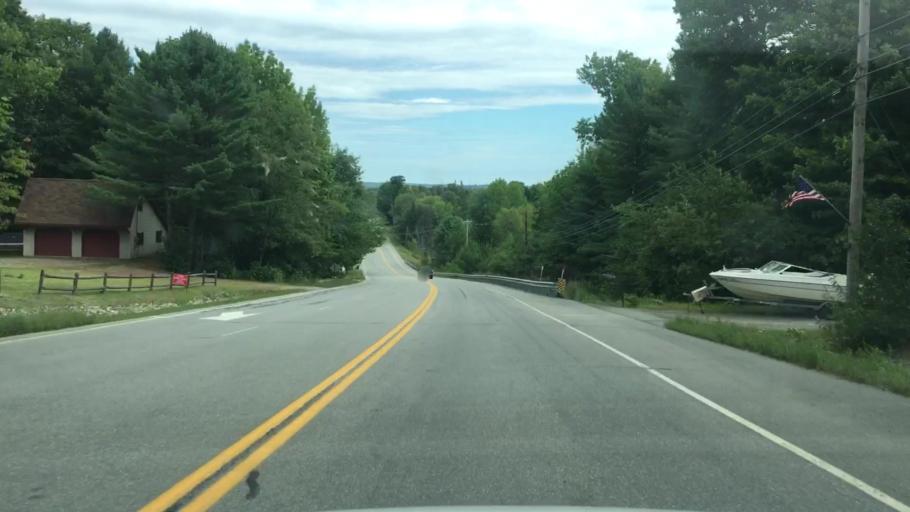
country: US
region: Maine
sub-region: Piscataquis County
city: Milo
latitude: 45.2451
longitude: -69.0066
